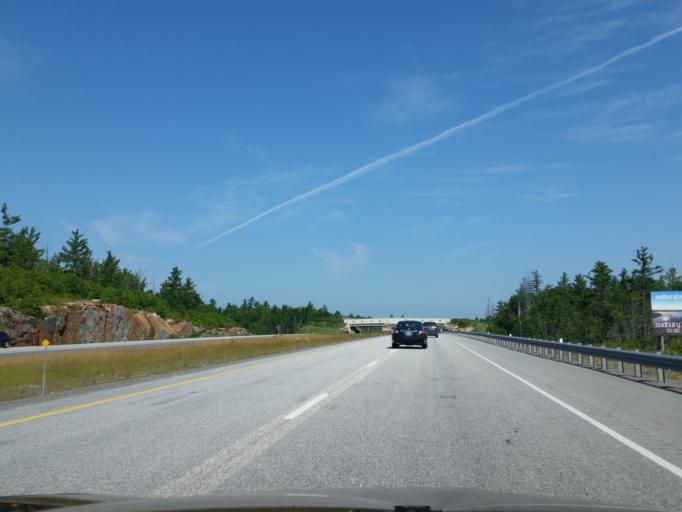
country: CA
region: Ontario
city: Greater Sudbury
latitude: 46.2347
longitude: -80.7790
